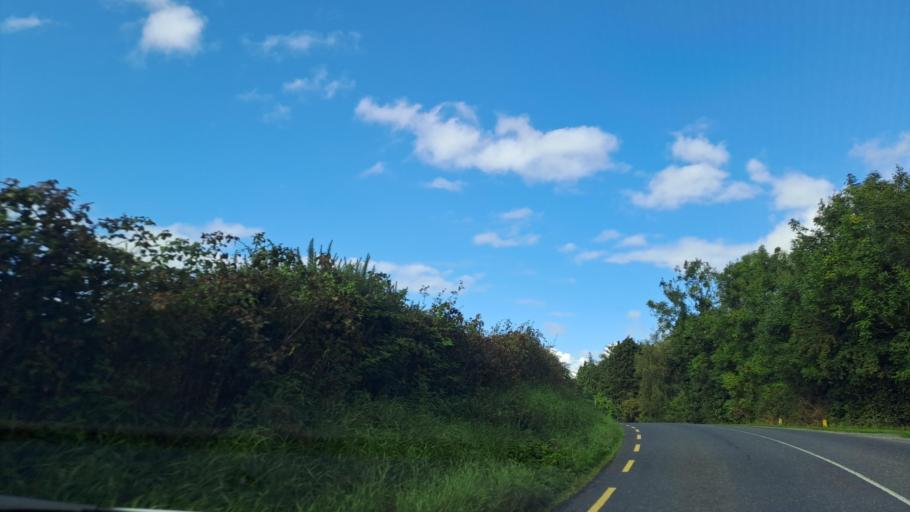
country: IE
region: Ulster
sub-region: An Cabhan
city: Kingscourt
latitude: 53.9495
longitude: -6.8396
